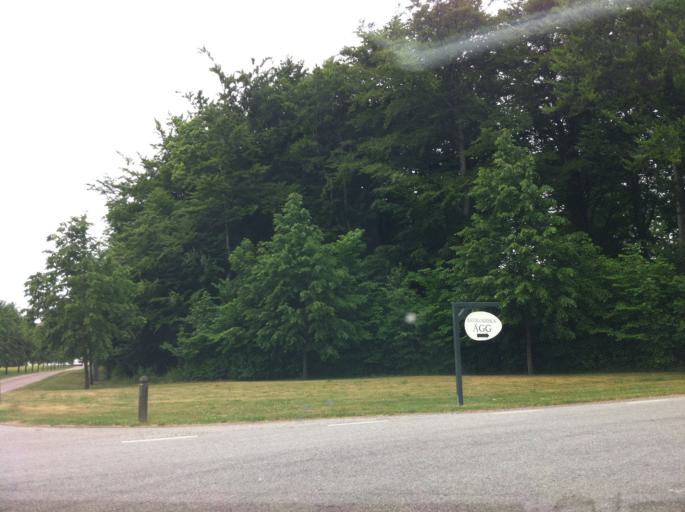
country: SE
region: Skane
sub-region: Hoors Kommun
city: Loberod
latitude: 55.7963
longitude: 13.4307
